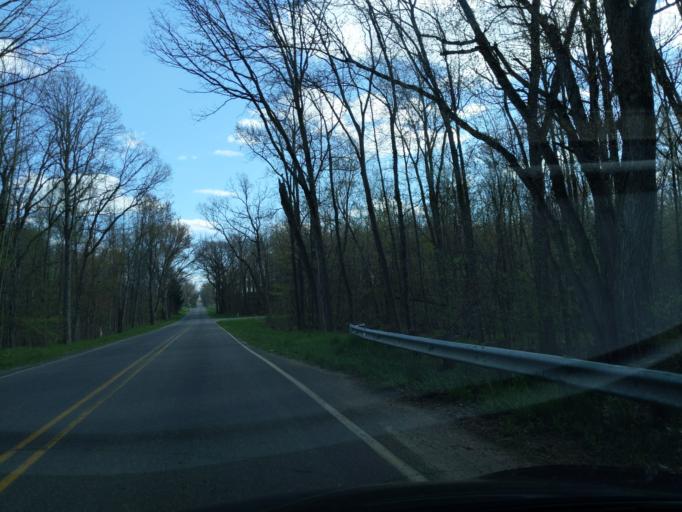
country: US
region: Michigan
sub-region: Ingham County
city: Leslie
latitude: 42.3908
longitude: -84.5417
